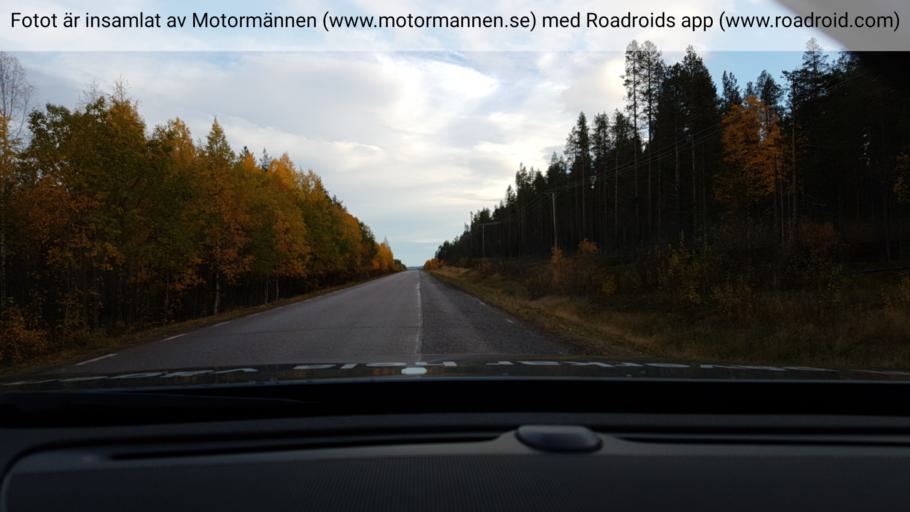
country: SE
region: Norrbotten
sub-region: Overkalix Kommun
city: OEverkalix
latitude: 67.0261
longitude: 22.5139
